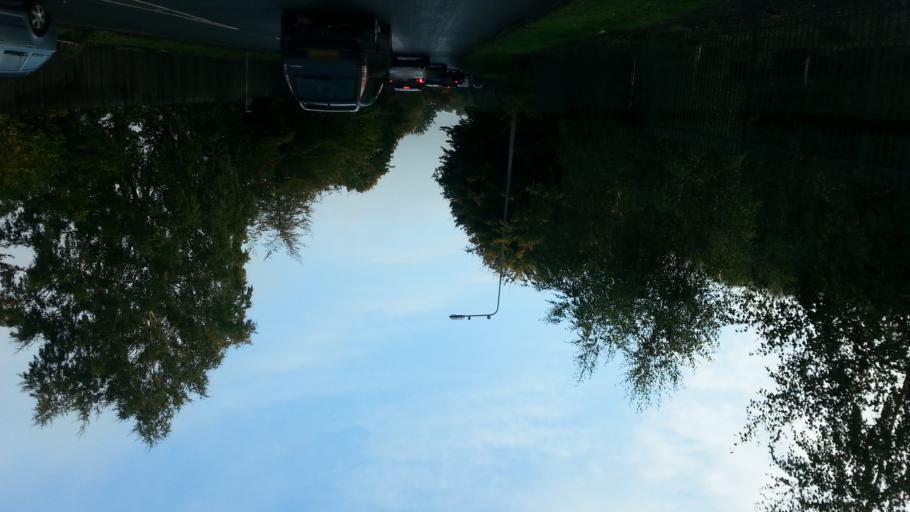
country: GB
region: England
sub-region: Worcestershire
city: Bromsgrove
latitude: 52.3217
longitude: -2.0597
